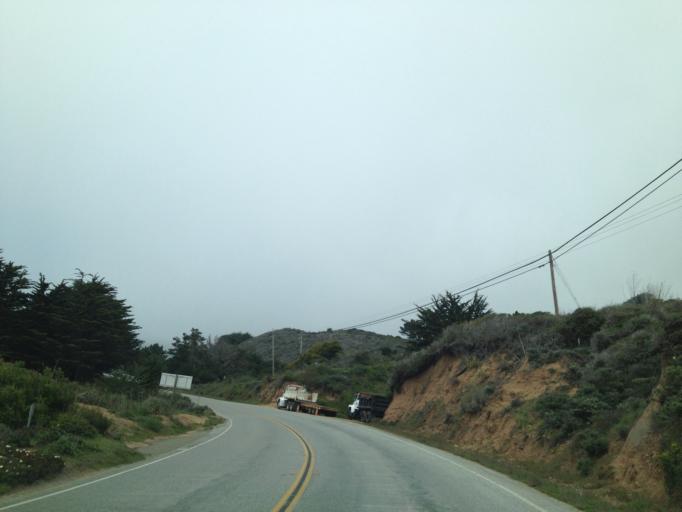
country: US
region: California
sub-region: Monterey County
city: Carmel-by-the-Sea
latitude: 36.4118
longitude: -121.9141
